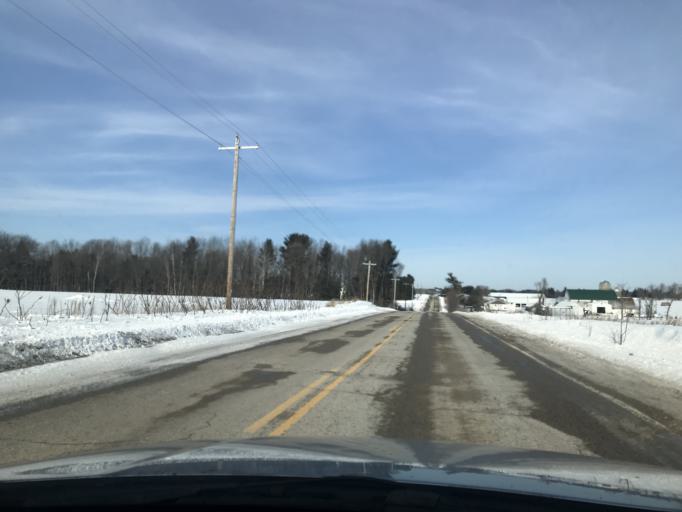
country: US
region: Wisconsin
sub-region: Oconto County
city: Oconto Falls
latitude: 45.1192
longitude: -88.1781
